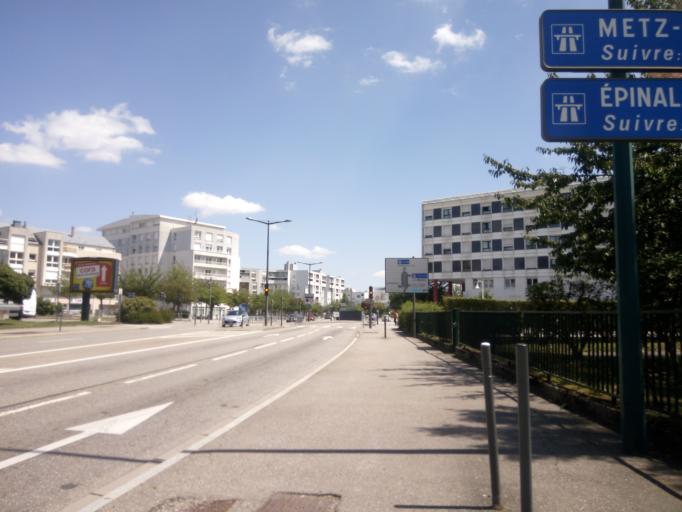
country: FR
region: Lorraine
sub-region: Departement de Meurthe-et-Moselle
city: Villers-les-Nancy
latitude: 48.6672
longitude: 6.1631
